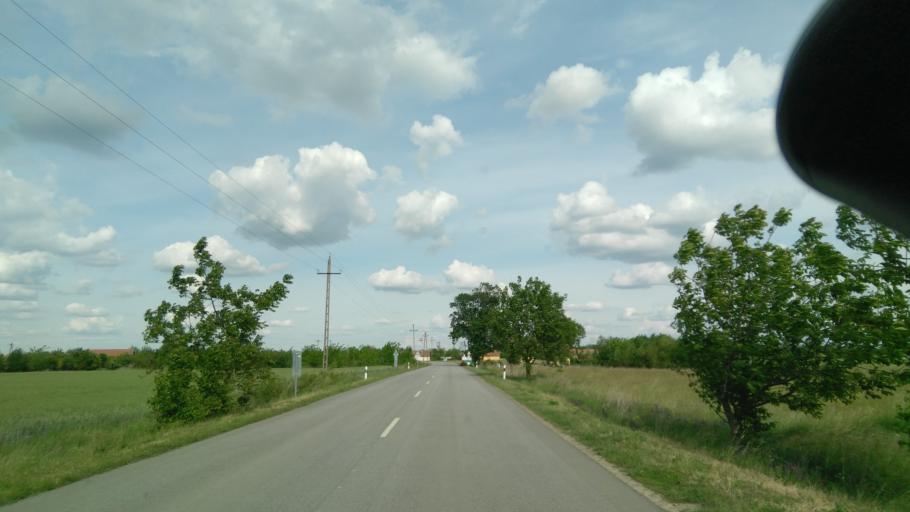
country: HU
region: Bekes
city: Battonya
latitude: 46.2914
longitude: 20.9975
